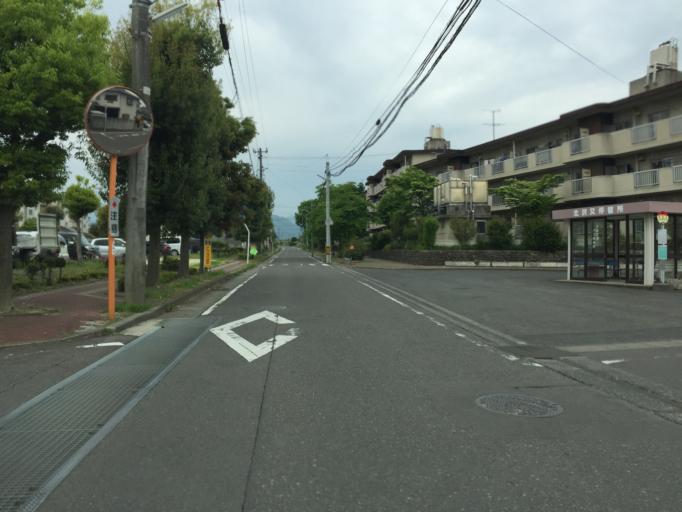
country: JP
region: Fukushima
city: Fukushima-shi
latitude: 37.7834
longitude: 140.4247
